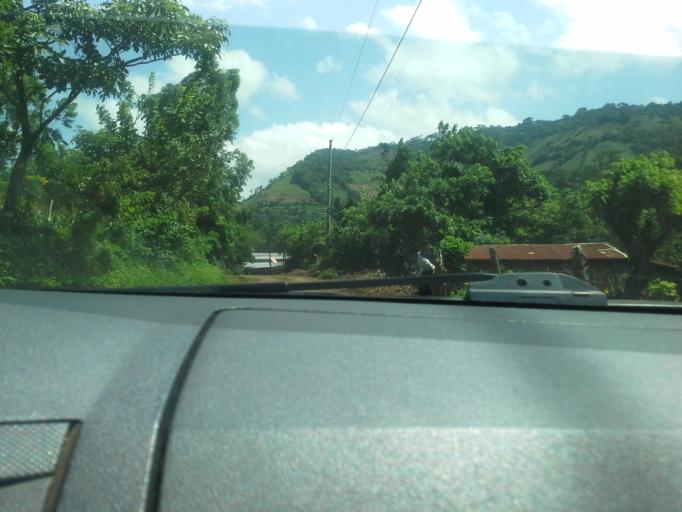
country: NI
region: Matagalpa
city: Terrabona
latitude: 12.7422
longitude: -85.9227
